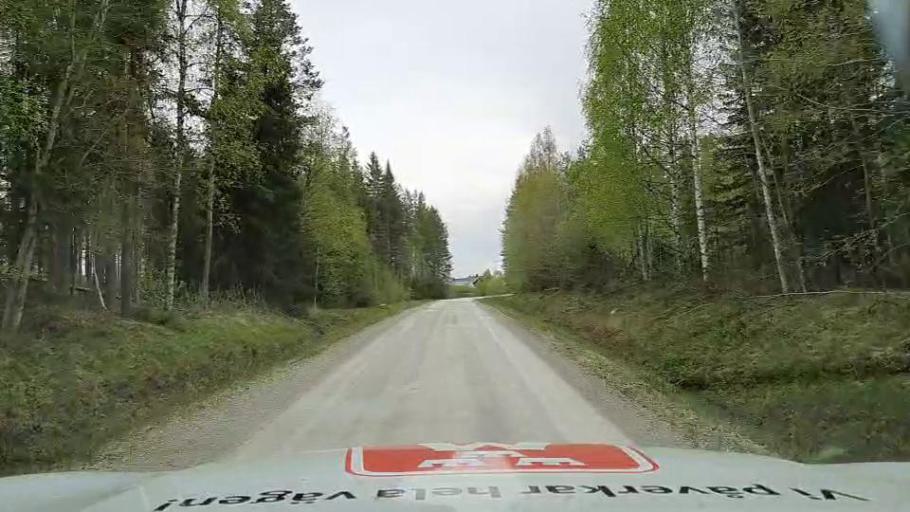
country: SE
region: Jaemtland
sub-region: Bergs Kommun
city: Hoverberg
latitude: 62.6848
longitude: 14.7746
